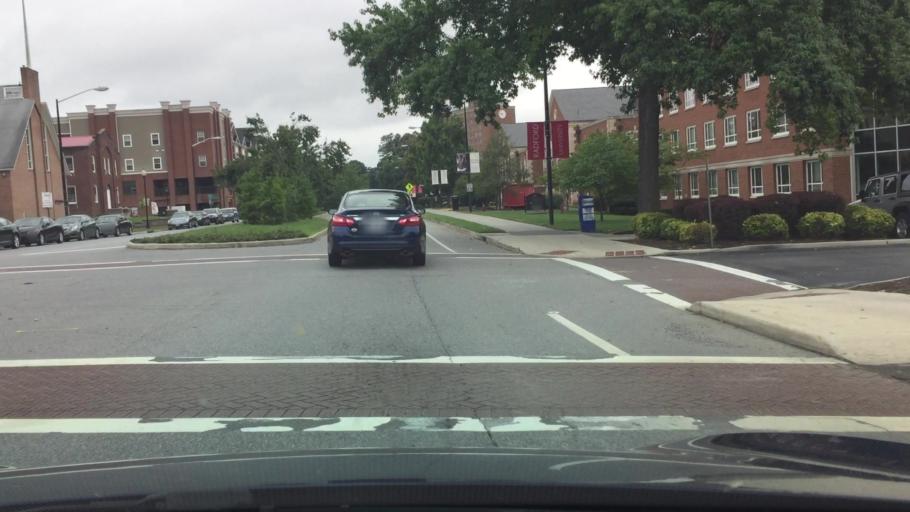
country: US
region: Virginia
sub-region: City of Radford
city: Radford
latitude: 37.1367
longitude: -80.5528
